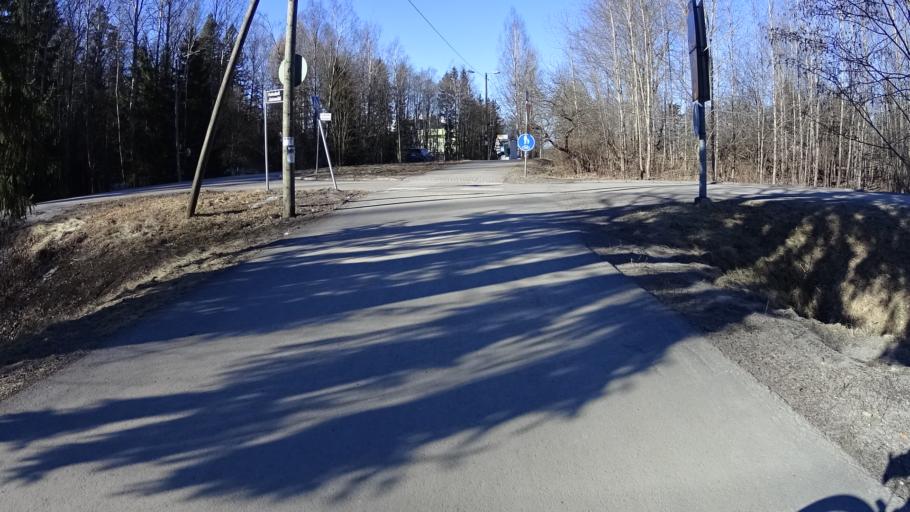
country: FI
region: Uusimaa
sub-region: Helsinki
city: Kauniainen
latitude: 60.2238
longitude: 24.6952
